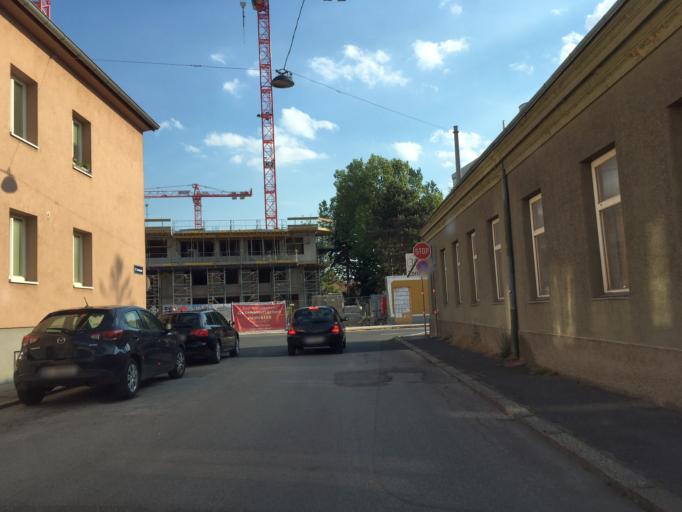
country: AT
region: Lower Austria
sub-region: Politischer Bezirk Modling
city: Vosendorf
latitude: 48.1382
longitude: 16.3228
